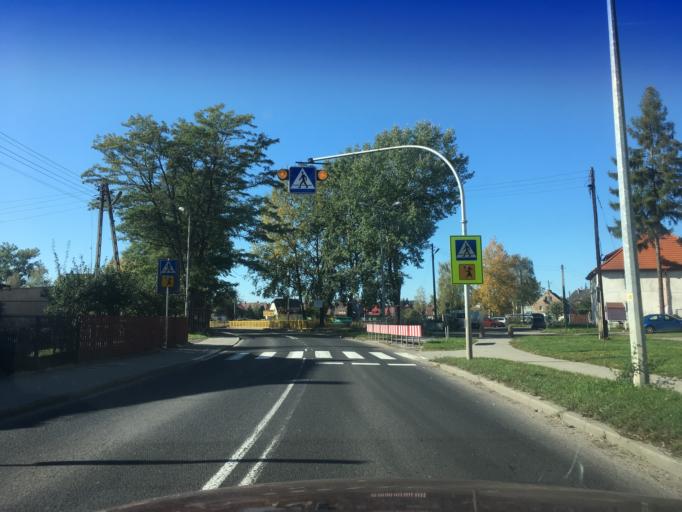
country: DE
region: Saxony
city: Hirschfelde
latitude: 50.9468
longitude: 14.9044
